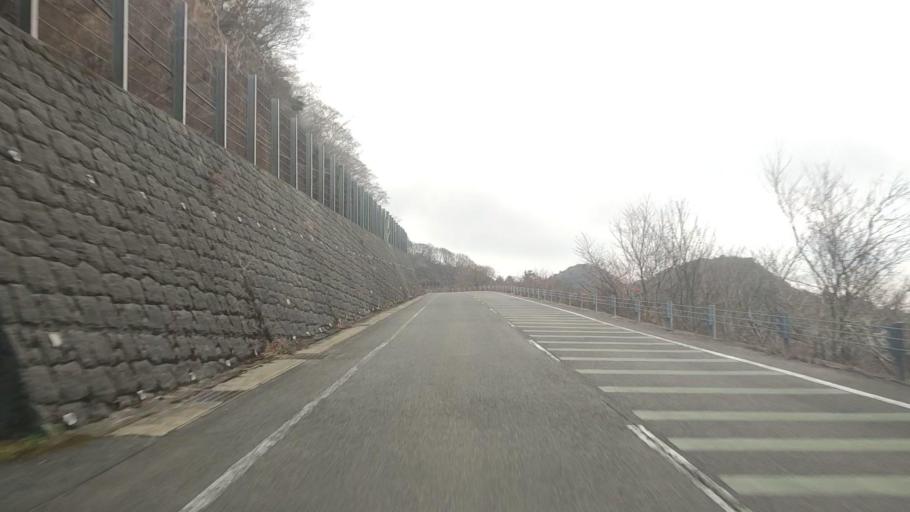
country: JP
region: Nagasaki
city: Shimabara
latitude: 32.7596
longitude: 130.2770
